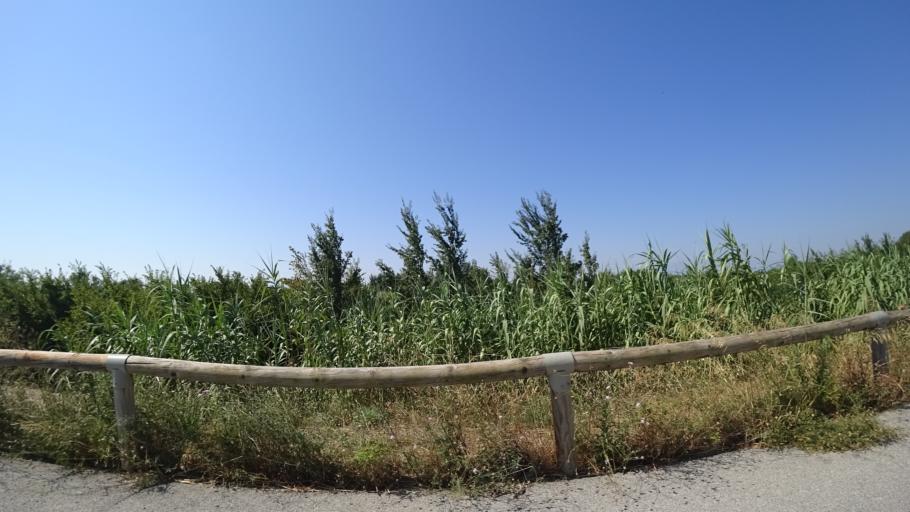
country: FR
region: Languedoc-Roussillon
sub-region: Departement des Pyrenees-Orientales
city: Pia
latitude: 42.7607
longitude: 2.9259
